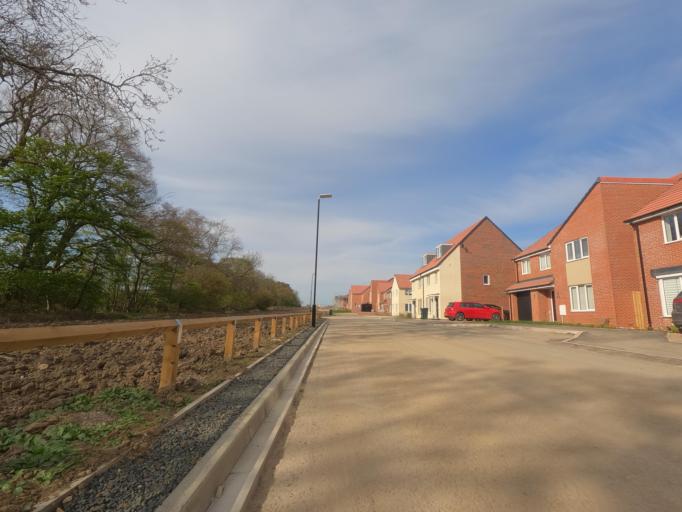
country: GB
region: England
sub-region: Newcastle upon Tyne
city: Dinnington
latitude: 55.0330
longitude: -1.6650
